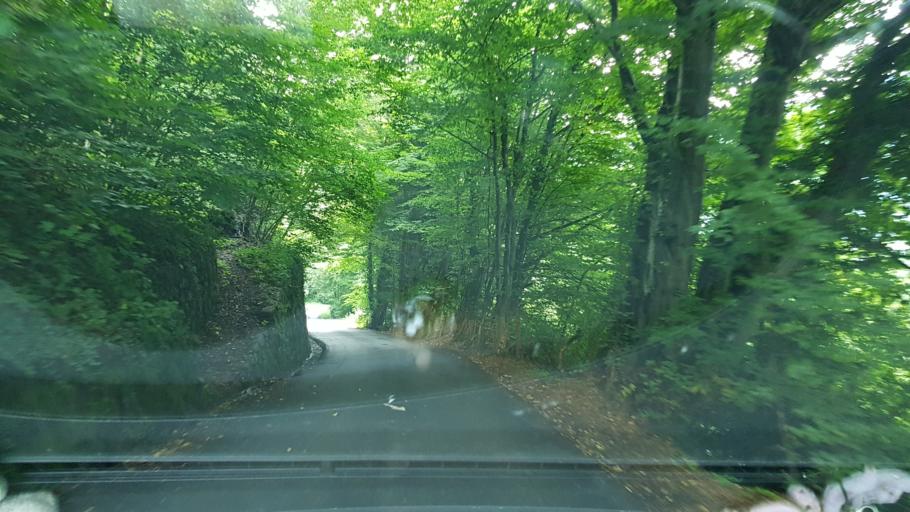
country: IT
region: Friuli Venezia Giulia
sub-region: Provincia di Udine
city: Cercivento
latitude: 46.5288
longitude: 12.9847
